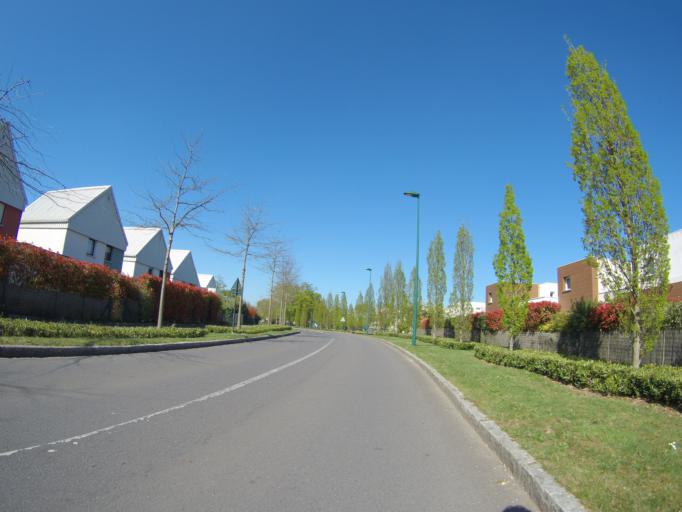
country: FR
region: Brittany
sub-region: Departement d'Ille-et-Vilaine
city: Vern-sur-Seiche
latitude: 48.0518
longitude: -1.6141
